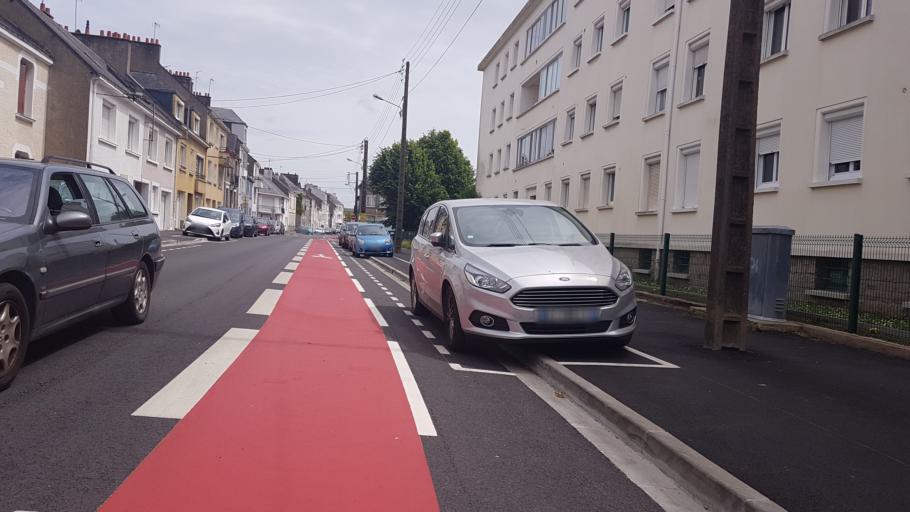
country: FR
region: Pays de la Loire
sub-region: Departement de la Loire-Atlantique
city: Saint-Nazaire
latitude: 47.2780
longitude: -2.2208
